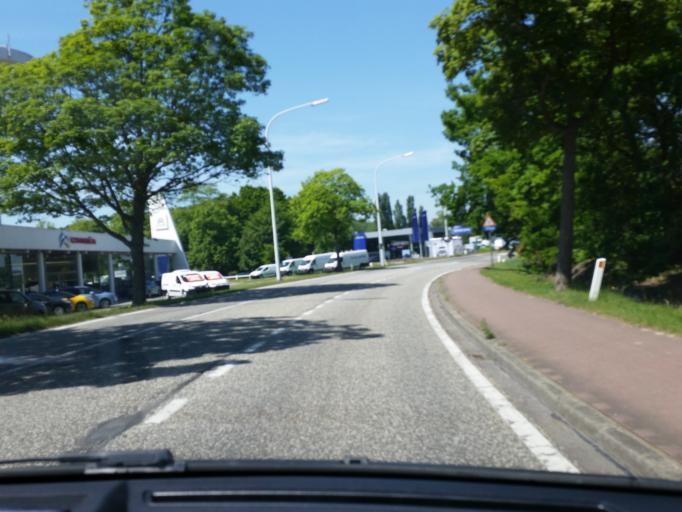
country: BE
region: Flanders
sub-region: Provincie Antwerpen
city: Mechelen
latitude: 51.0588
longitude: 4.4599
